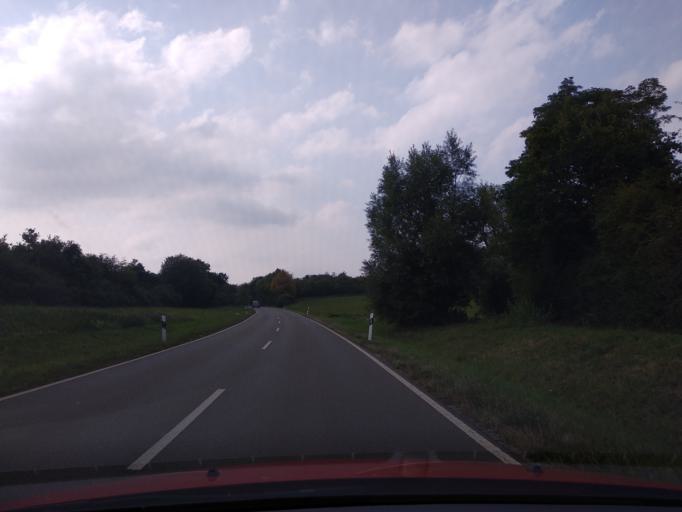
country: DE
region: Hesse
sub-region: Regierungsbezirk Kassel
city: Calden
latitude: 51.3765
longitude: 9.3799
